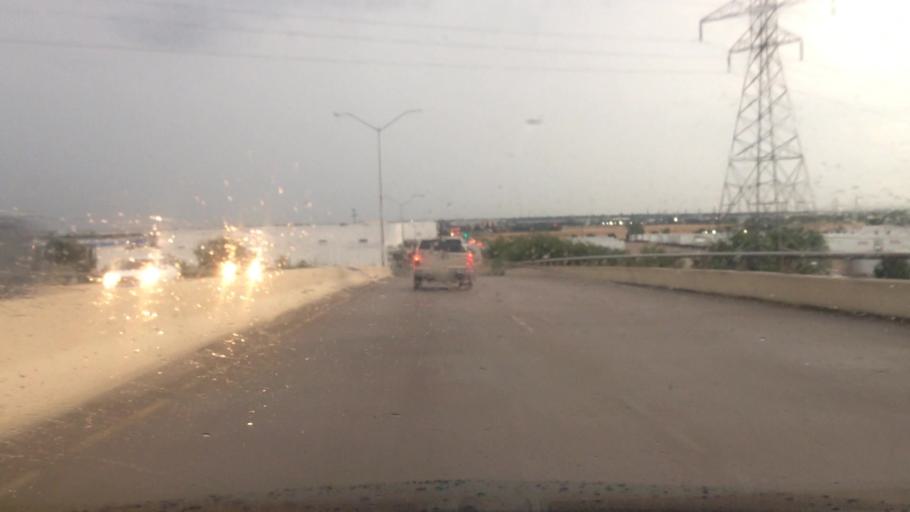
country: US
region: Texas
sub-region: Tarrant County
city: Blue Mound
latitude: 32.8247
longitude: -97.3312
